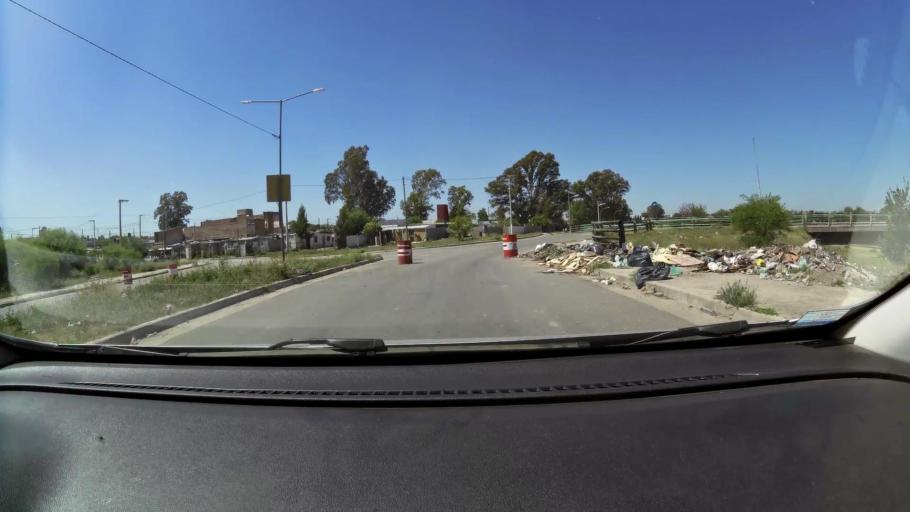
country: AR
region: Cordoba
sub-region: Departamento de Capital
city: Cordoba
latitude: -31.4107
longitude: -64.1407
